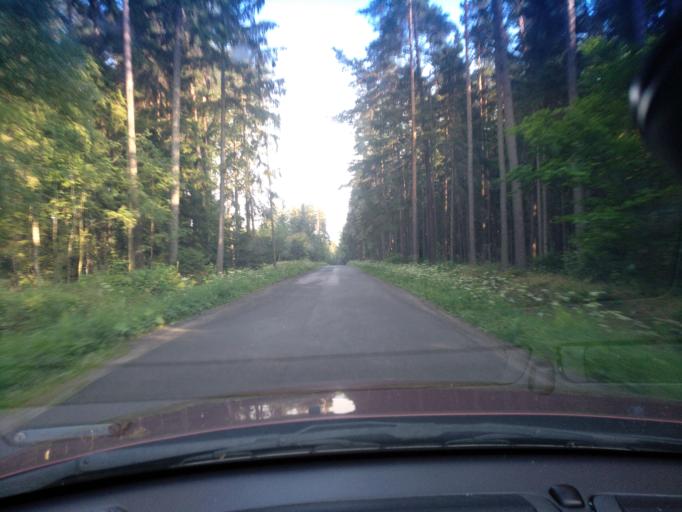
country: PL
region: Lower Silesian Voivodeship
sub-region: Powiat lubanski
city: Lesna
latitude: 50.9676
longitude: 15.2968
